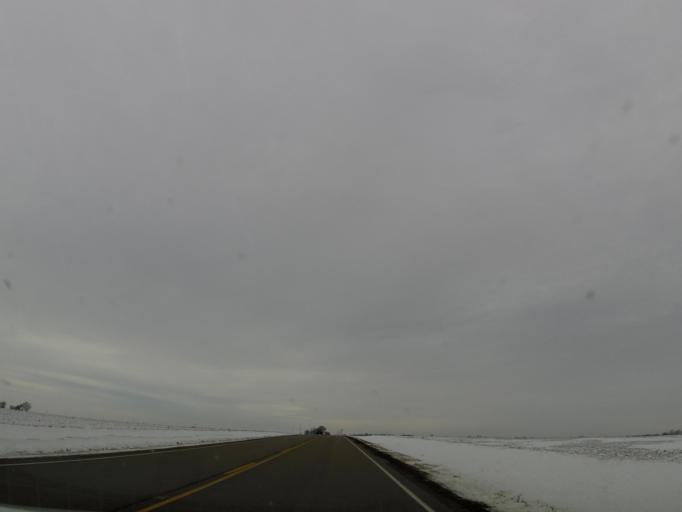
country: US
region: Illinois
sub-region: Putnam County
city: Granville
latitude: 41.2578
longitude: -89.1932
